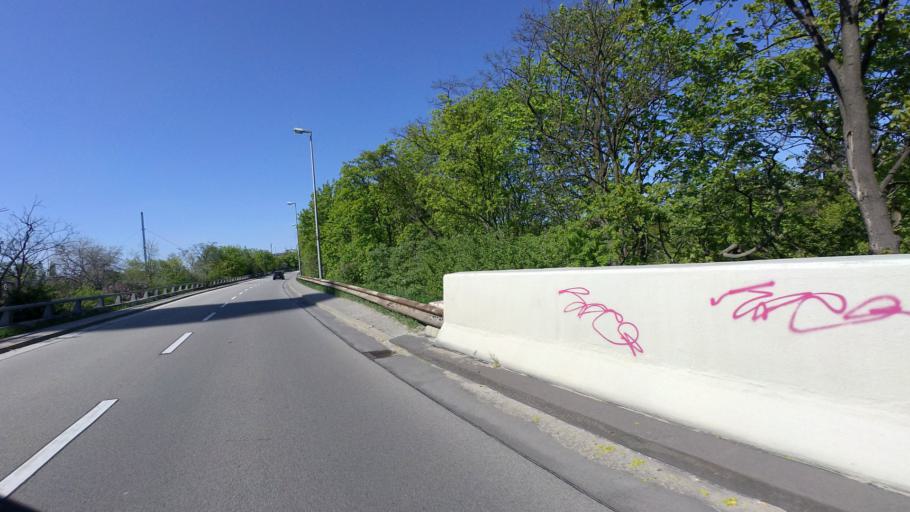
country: DE
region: Berlin
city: Wilmersdorf Bezirk
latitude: 52.4827
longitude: 13.3089
